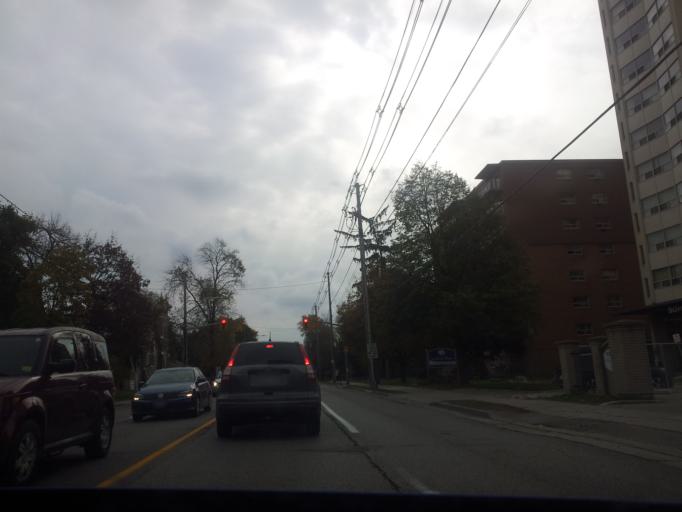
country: CA
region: Ontario
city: London
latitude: 43.0119
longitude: -81.2644
